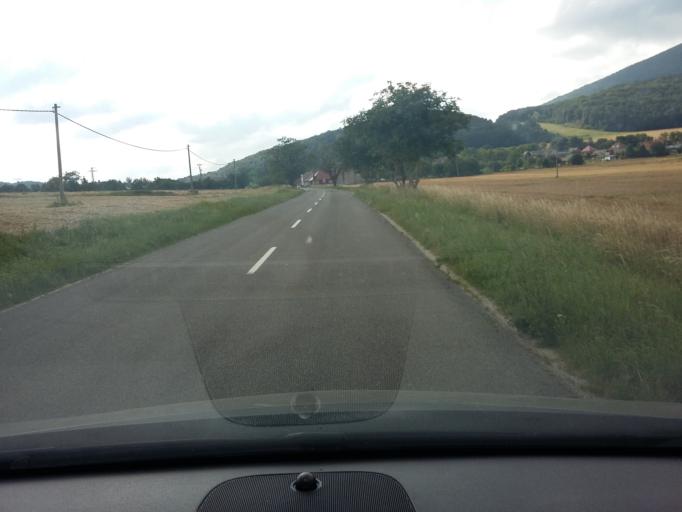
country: SK
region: Trnavsky
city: Smolenice
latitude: 48.5434
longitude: 17.3857
